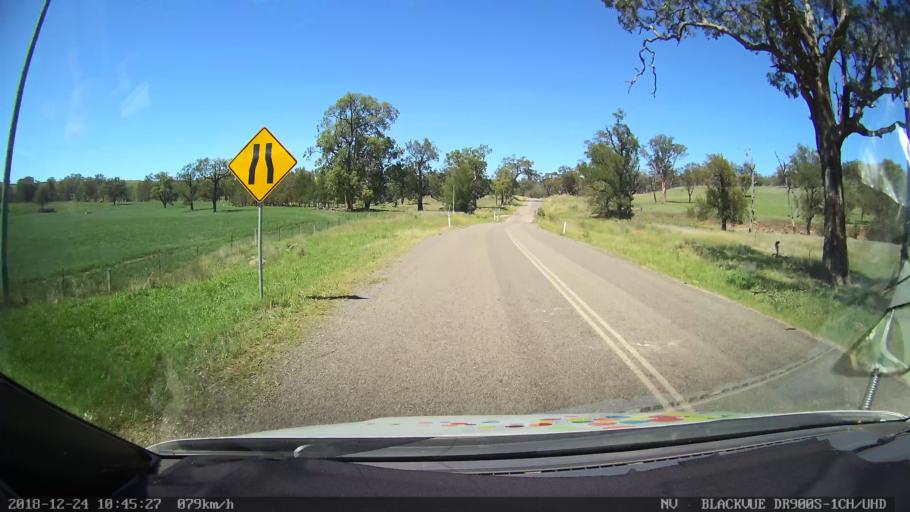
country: AU
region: New South Wales
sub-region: Upper Hunter Shire
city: Merriwa
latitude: -31.9032
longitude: 150.4356
